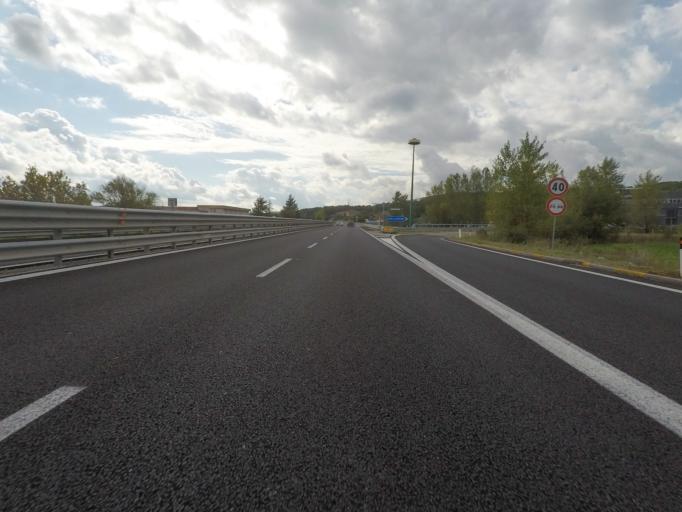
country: IT
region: Tuscany
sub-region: Provincia di Siena
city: Serre di Rapolano
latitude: 43.2685
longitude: 11.6291
